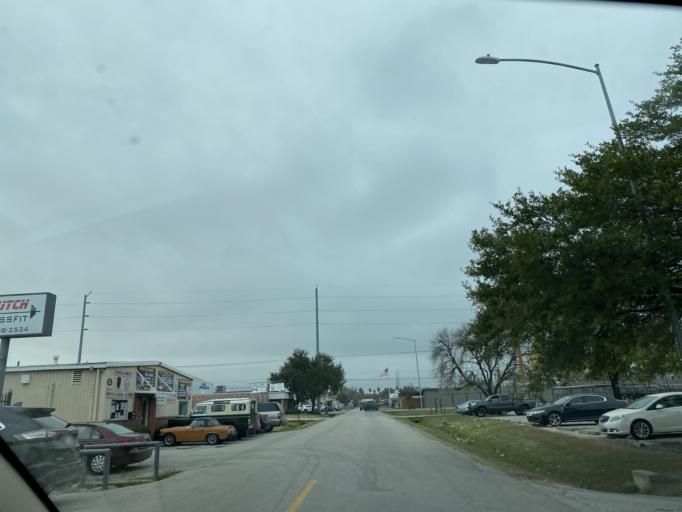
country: US
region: Texas
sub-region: Harris County
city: Bellaire
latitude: 29.7288
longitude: -95.4791
